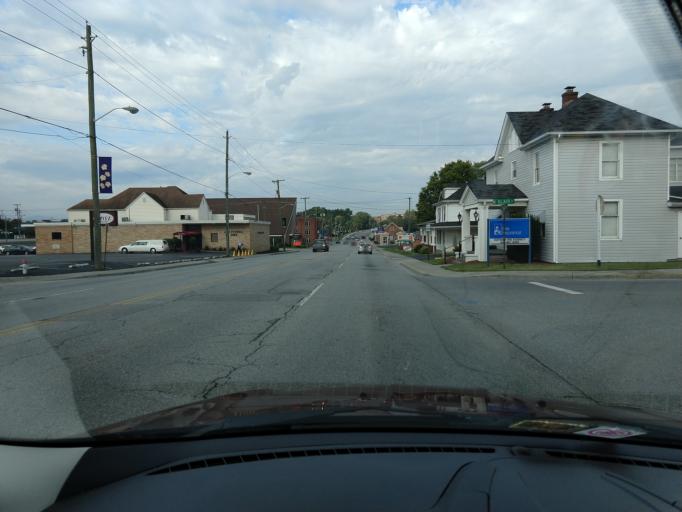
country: US
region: Virginia
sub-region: Roanoke County
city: Vinton
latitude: 37.2816
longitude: -79.8975
